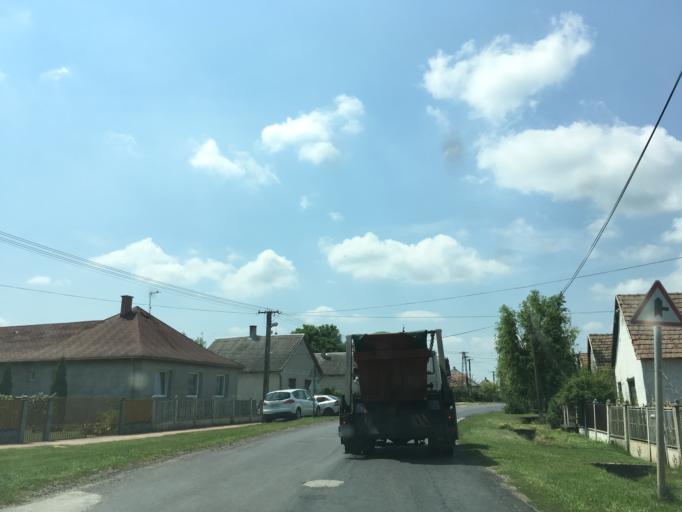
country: HU
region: Szabolcs-Szatmar-Bereg
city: Nyirlugos
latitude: 47.6578
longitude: 22.0368
